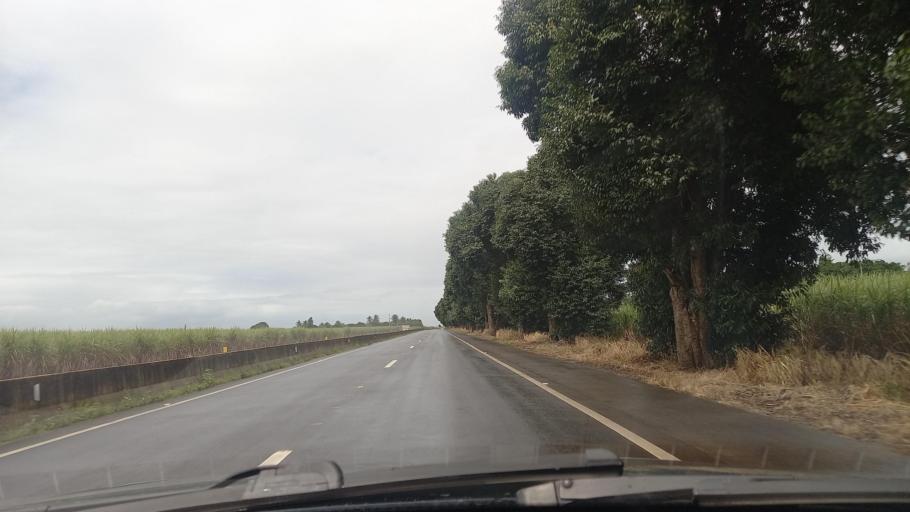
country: BR
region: Alagoas
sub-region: Campo Alegre
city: Campo Alegre
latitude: -9.8127
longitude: -36.2549
